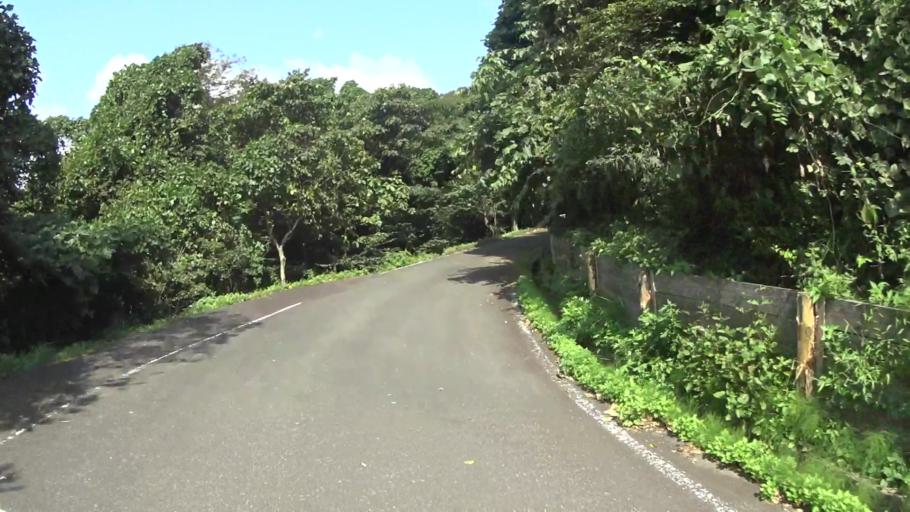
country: JP
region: Kyoto
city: Miyazu
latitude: 35.6588
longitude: 135.2353
